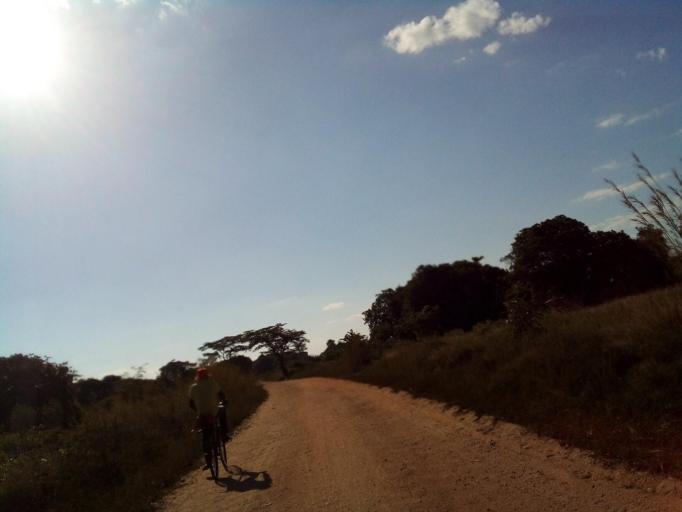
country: MZ
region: Zambezia
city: Quelimane
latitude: -17.5341
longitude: 36.6216
